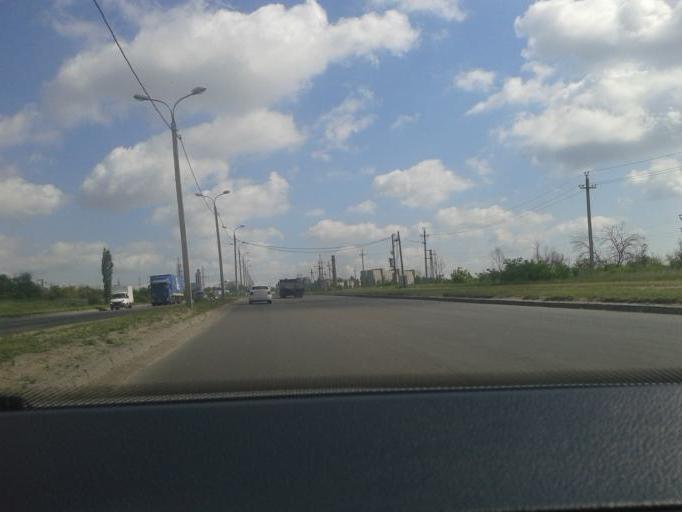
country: RU
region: Volgograd
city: Volgograd
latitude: 48.7407
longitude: 44.4618
